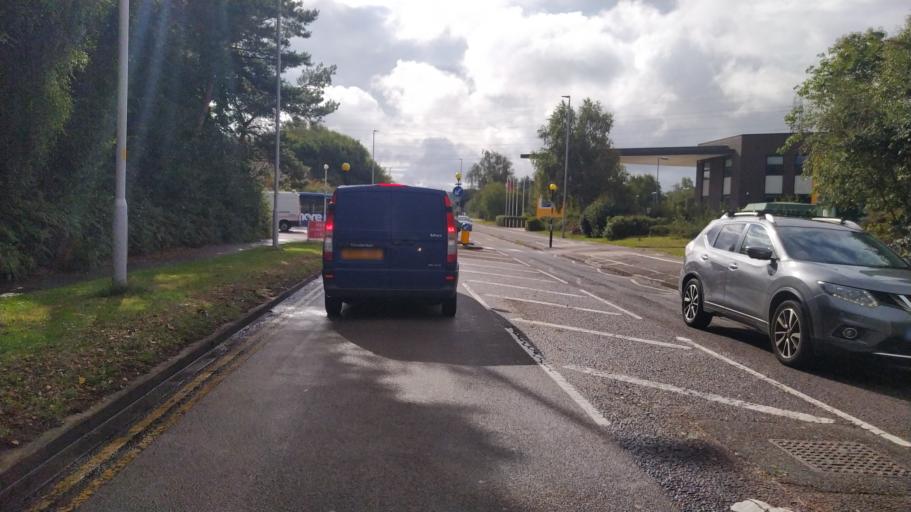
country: GB
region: England
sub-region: Poole
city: Canford Heath
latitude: 50.7492
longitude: -1.9660
